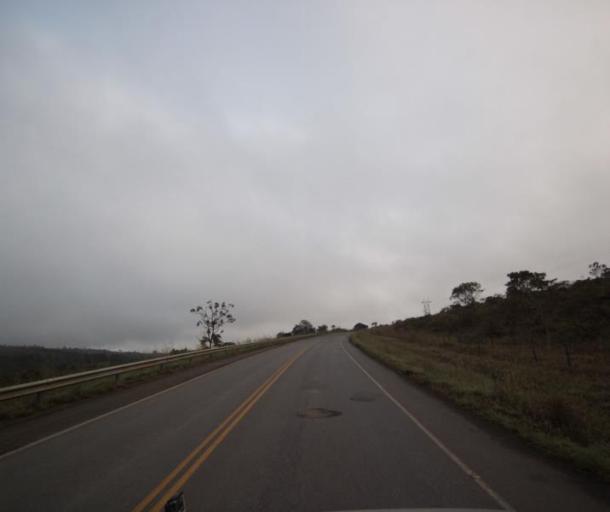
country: BR
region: Goias
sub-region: Pirenopolis
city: Pirenopolis
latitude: -15.8111
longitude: -48.7823
